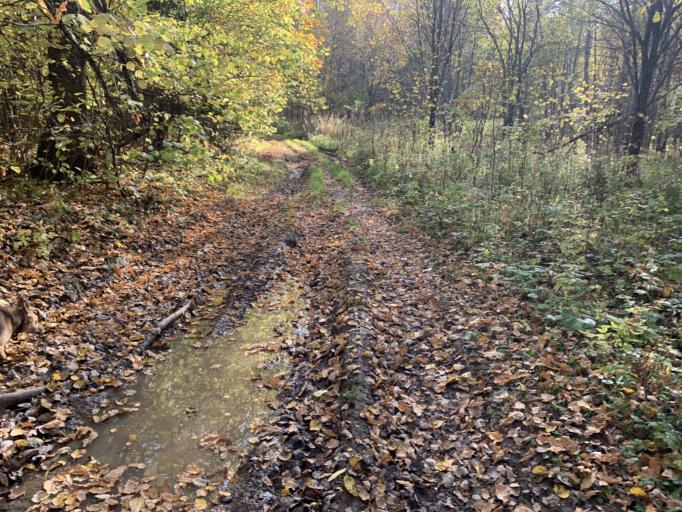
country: RU
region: Jaroslavl
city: Porech'ye-Rybnoye
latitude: 57.0029
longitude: 39.4055
